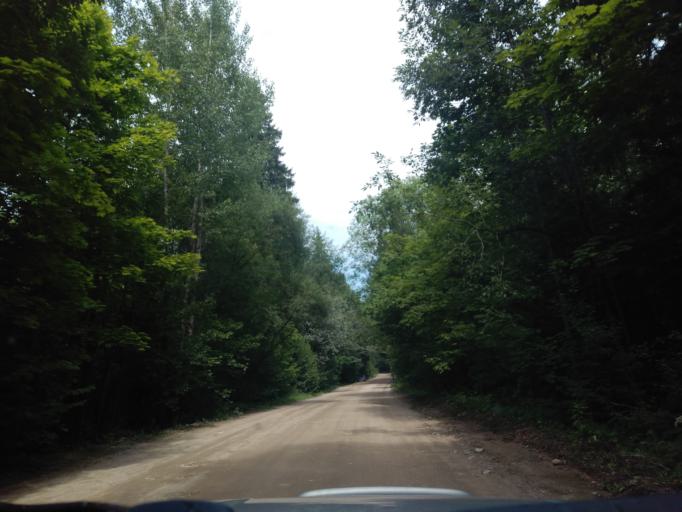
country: BY
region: Minsk
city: Khatsyezhyna
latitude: 53.9003
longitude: 27.2819
